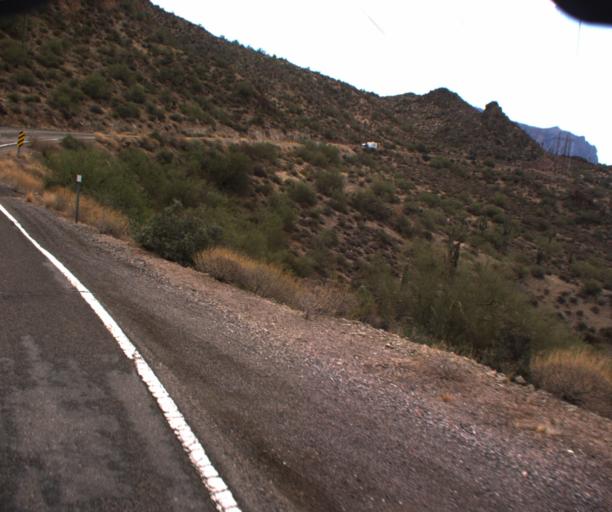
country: US
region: Arizona
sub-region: Pinal County
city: Apache Junction
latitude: 33.5123
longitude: -111.4563
